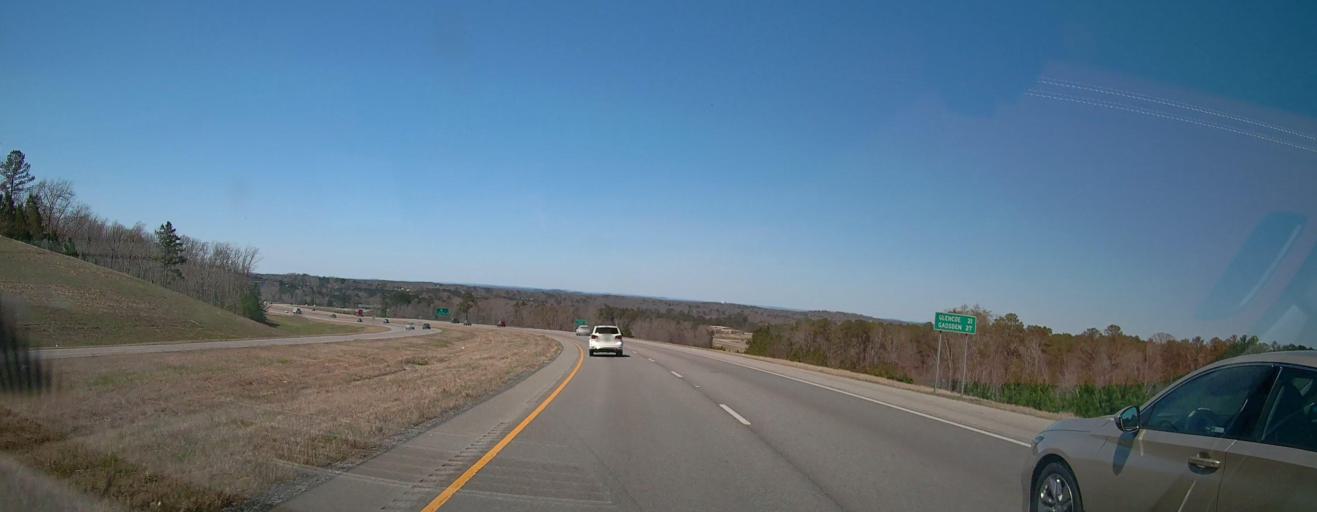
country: US
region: Alabama
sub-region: Calhoun County
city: Saks
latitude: 33.7016
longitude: -85.8108
